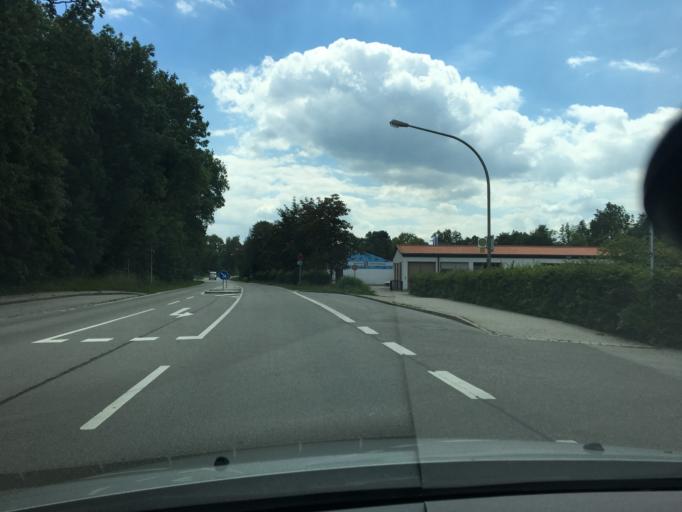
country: DE
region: Bavaria
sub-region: Lower Bavaria
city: Vilsbiburg
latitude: 48.4427
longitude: 12.3535
